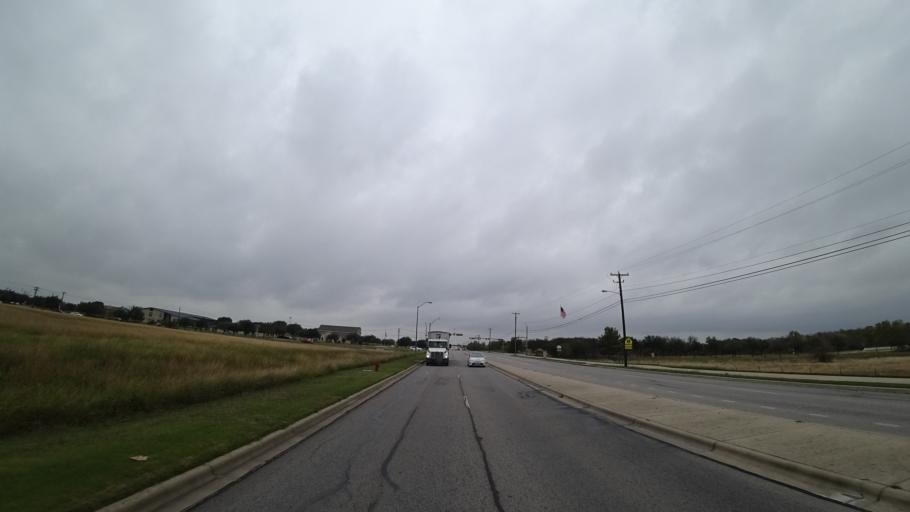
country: US
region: Texas
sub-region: Travis County
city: Pflugerville
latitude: 30.4585
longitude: -97.6149
